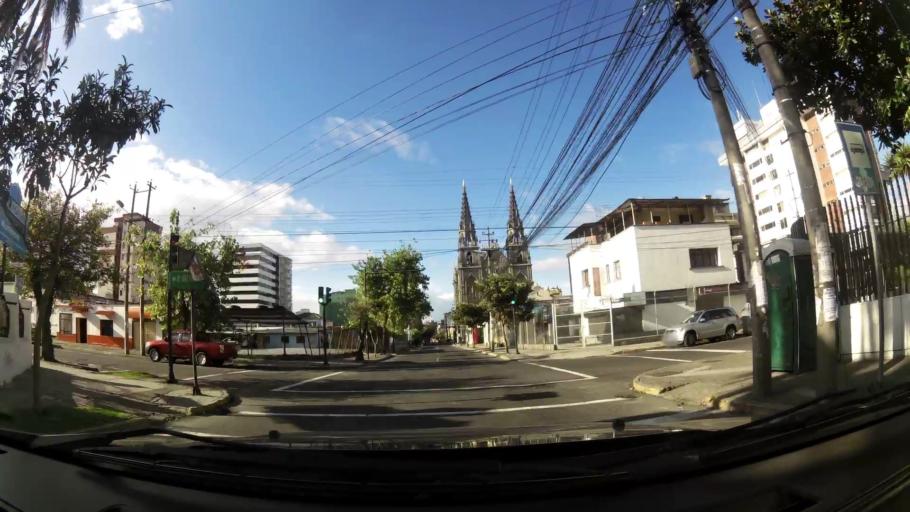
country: EC
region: Pichincha
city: Quito
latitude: -0.2058
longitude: -78.4970
